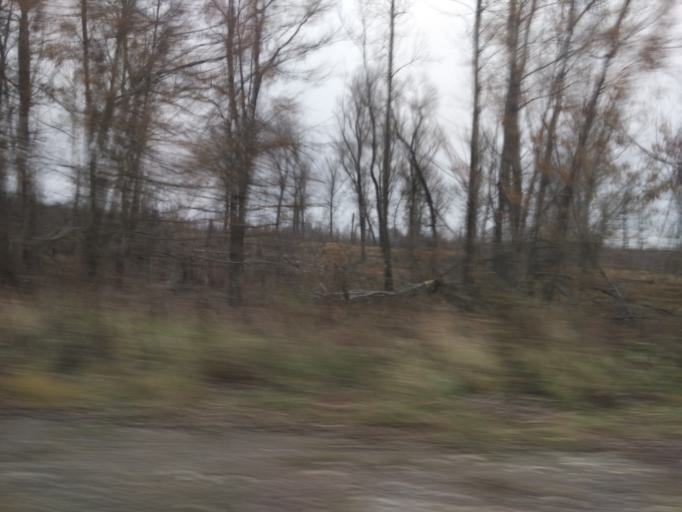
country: RU
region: Kirov
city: Krasnaya Polyana
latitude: 56.2482
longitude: 51.2083
